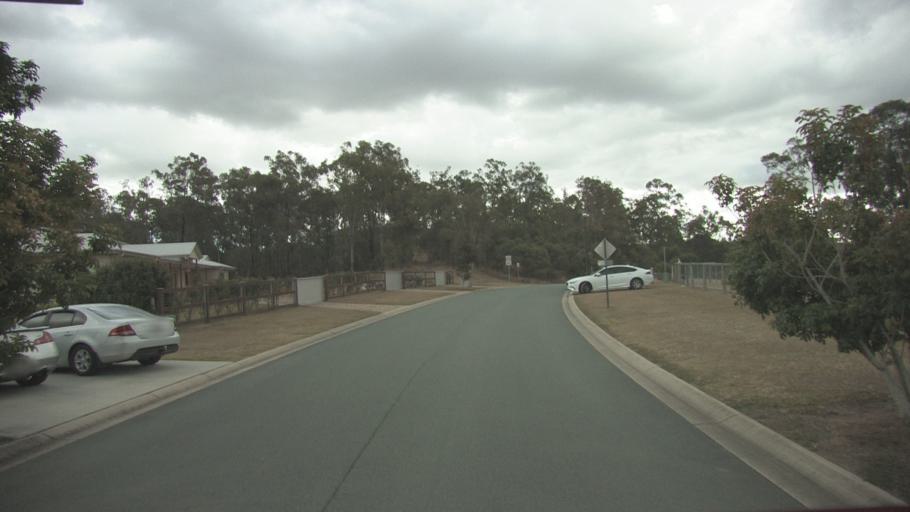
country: AU
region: Queensland
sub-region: Logan
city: Cedar Vale
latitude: -27.8675
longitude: 153.0767
